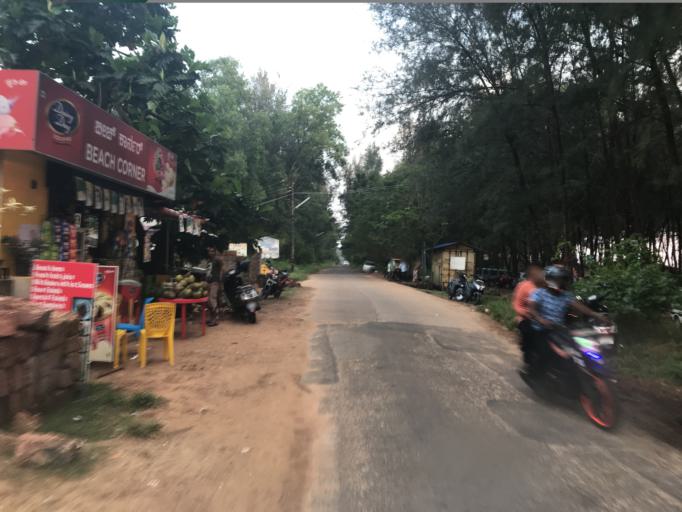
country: IN
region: Karnataka
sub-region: Dakshina Kannada
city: Mangalore
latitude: 12.8878
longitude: 74.8162
